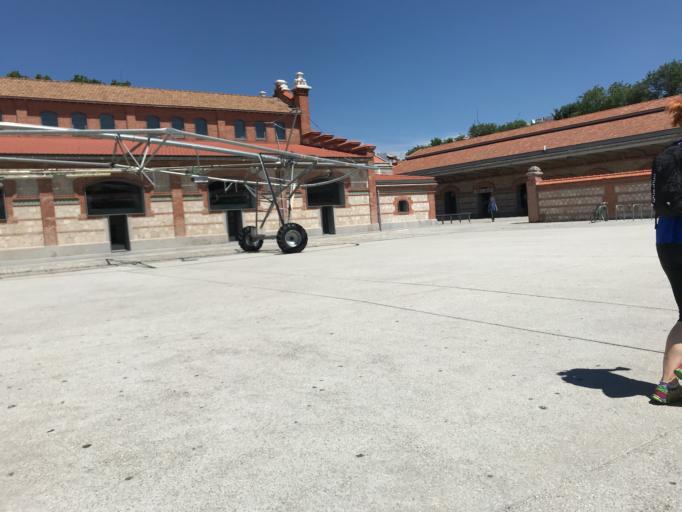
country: ES
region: Madrid
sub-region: Provincia de Madrid
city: Usera
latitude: 40.3921
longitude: -3.6981
